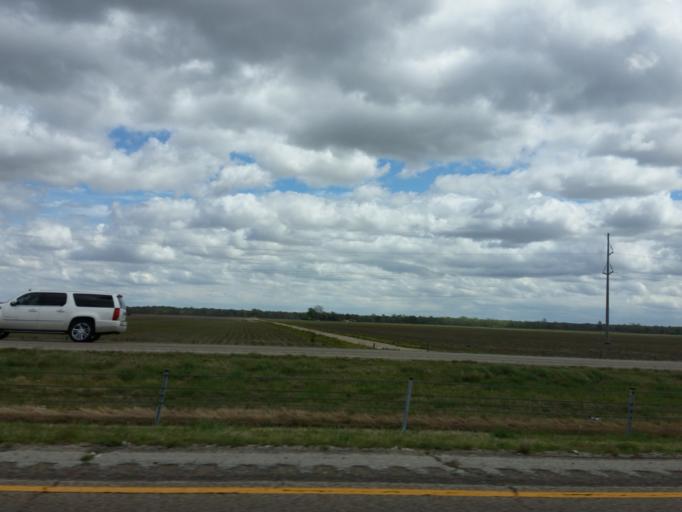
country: US
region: Arkansas
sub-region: Poinsett County
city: Trumann
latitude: 35.5943
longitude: -90.4968
